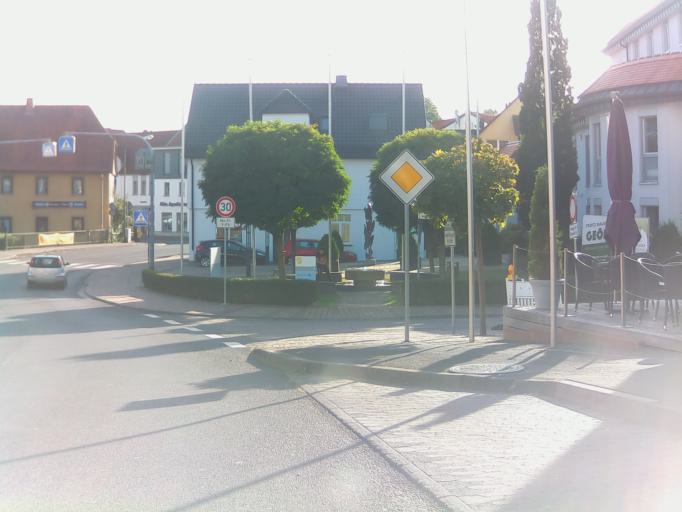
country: DE
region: Hesse
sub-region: Regierungsbezirk Kassel
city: Flieden
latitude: 50.4234
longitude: 9.5662
